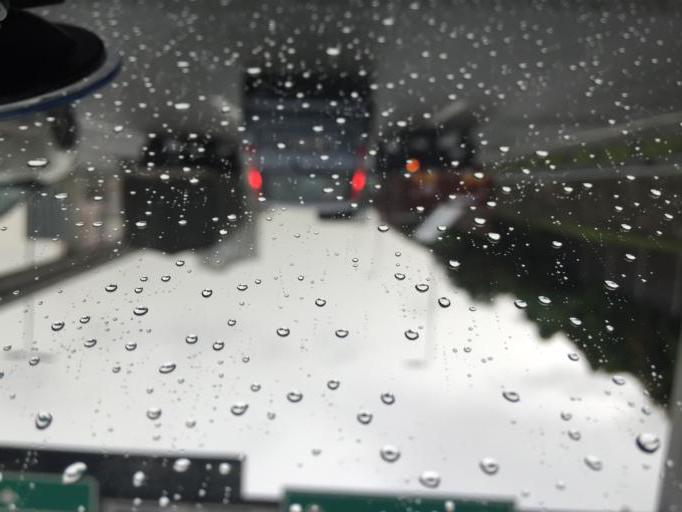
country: MY
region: Selangor
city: Subang Jaya
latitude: 3.0633
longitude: 101.5883
